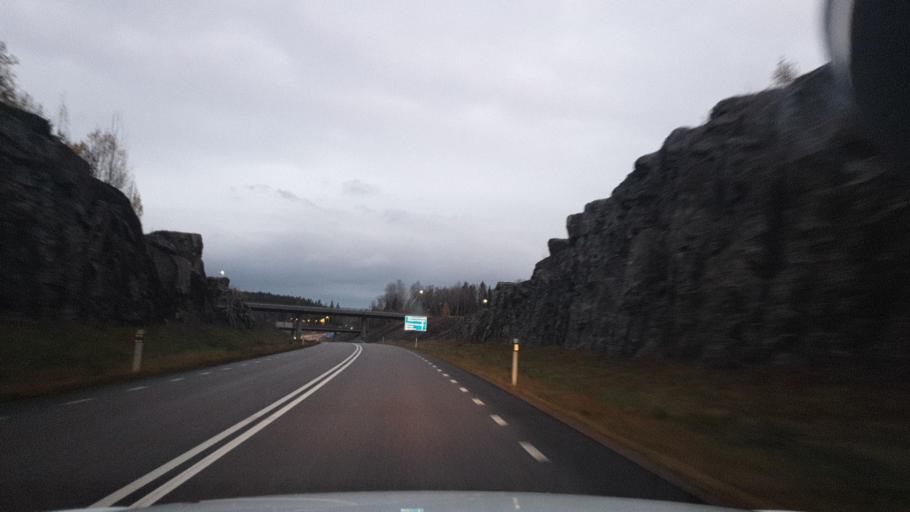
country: SE
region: Vaermland
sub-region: Eda Kommun
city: Amotfors
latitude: 59.7753
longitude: 12.3755
